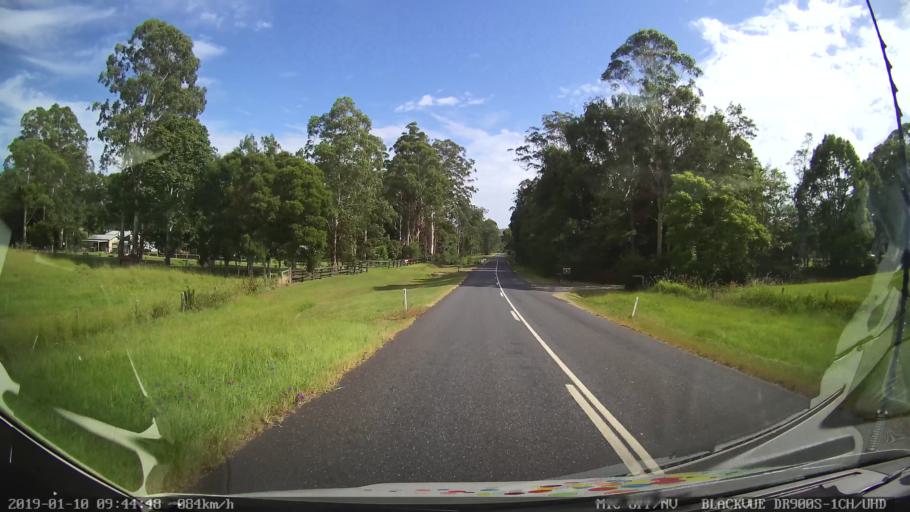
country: AU
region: New South Wales
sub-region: Coffs Harbour
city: Nana Glen
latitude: -30.1125
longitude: 153.0034
